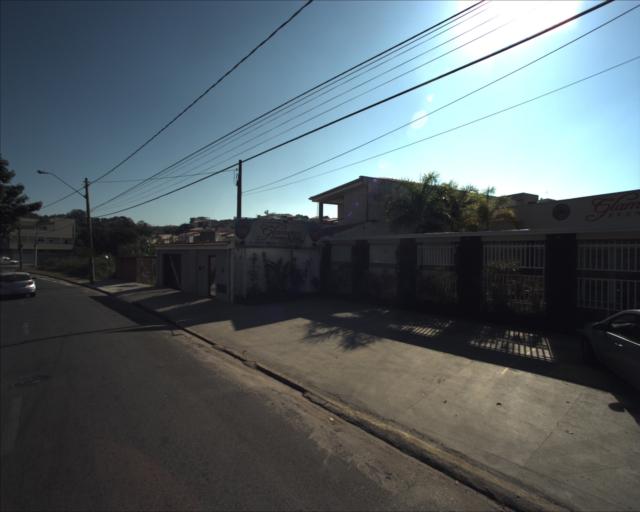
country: BR
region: Sao Paulo
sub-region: Sorocaba
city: Sorocaba
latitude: -23.5075
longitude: -47.4329
